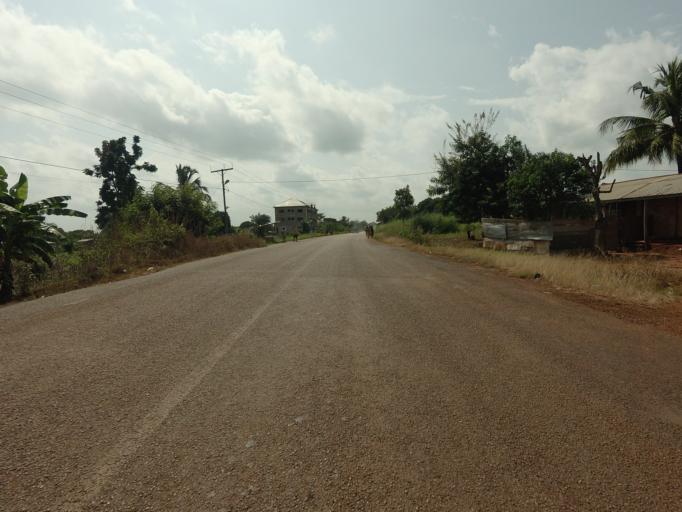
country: TG
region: Maritime
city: Tsevie
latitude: 6.3662
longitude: 0.8516
